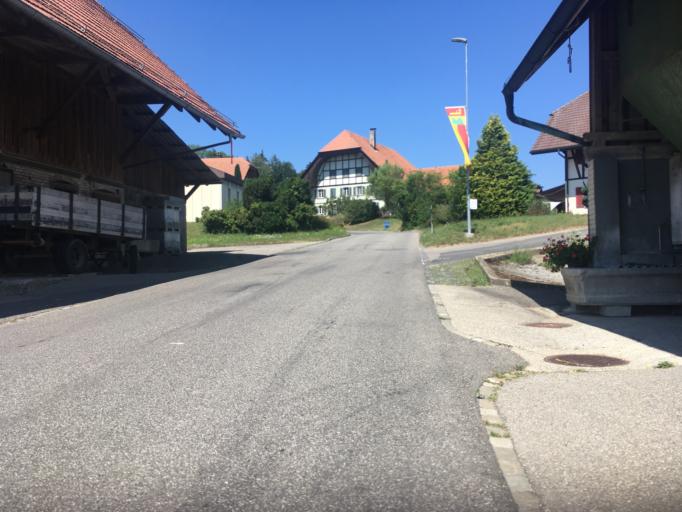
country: CH
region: Solothurn
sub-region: Bezirk Bucheggberg
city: Messen
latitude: 47.0862
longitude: 7.4693
